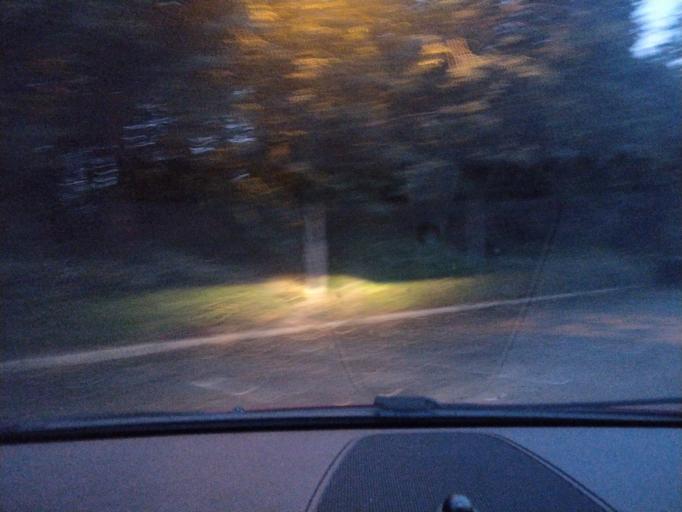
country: GB
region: England
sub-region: Lancashire
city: Ormskirk
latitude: 53.5635
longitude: -2.8690
